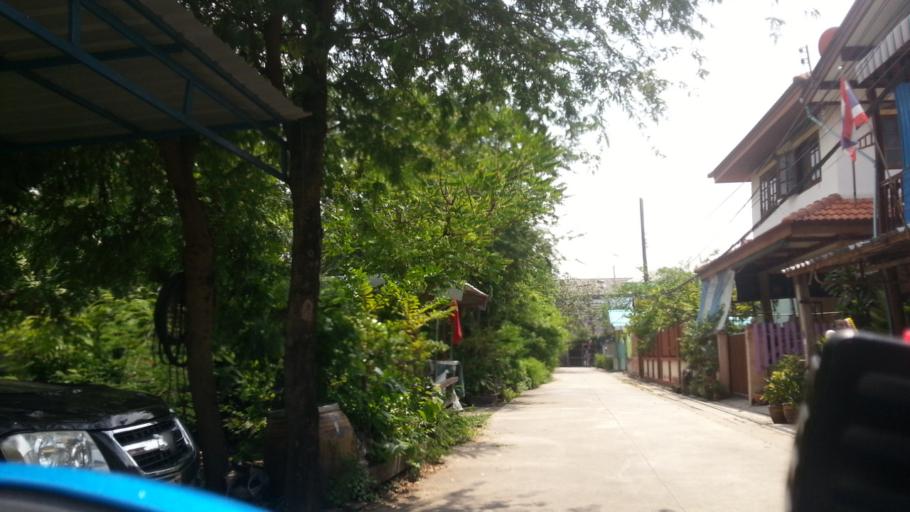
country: TH
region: Pathum Thani
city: Ban Rangsit
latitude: 14.0553
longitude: 100.8267
